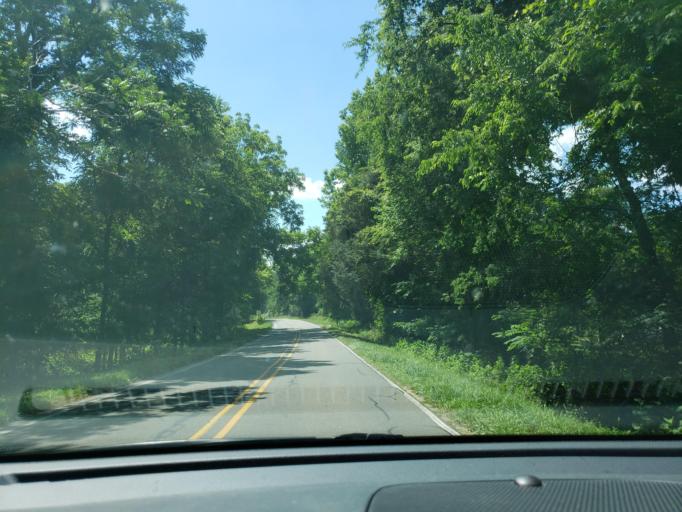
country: US
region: North Carolina
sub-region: Orange County
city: Chapel Hill
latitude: 36.0017
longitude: -79.0276
